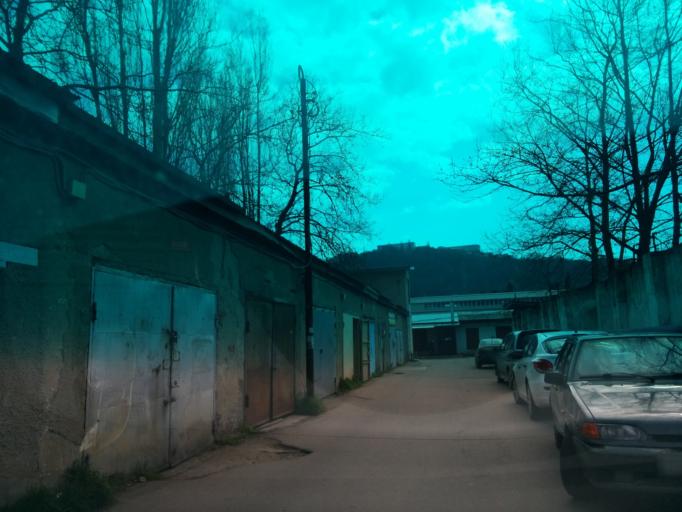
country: RU
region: Krasnodarskiy
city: Tuapse
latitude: 44.0956
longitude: 39.0807
